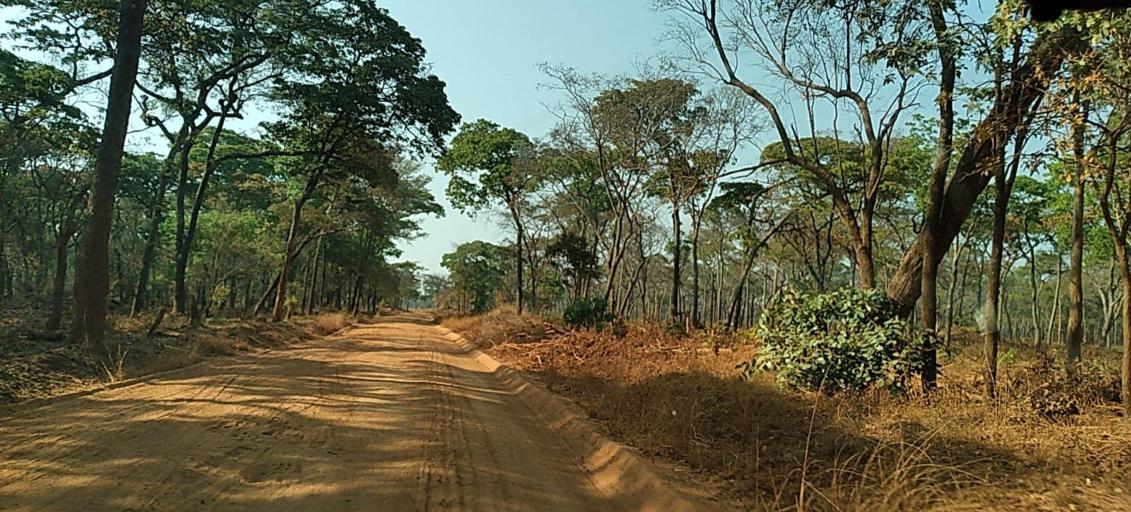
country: ZM
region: North-Western
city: Kasempa
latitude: -13.6184
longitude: 25.9801
